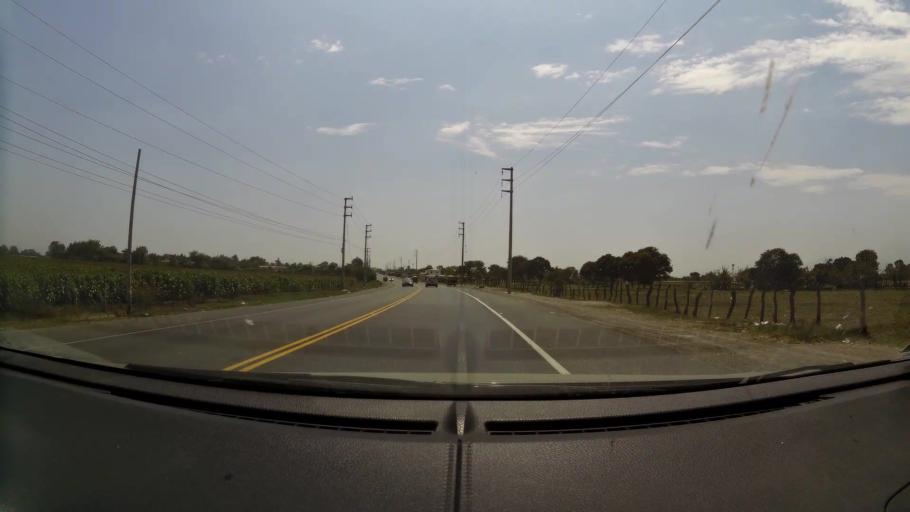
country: PE
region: La Libertad
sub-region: Chepen
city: Chepen
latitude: -7.1843
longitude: -79.4325
